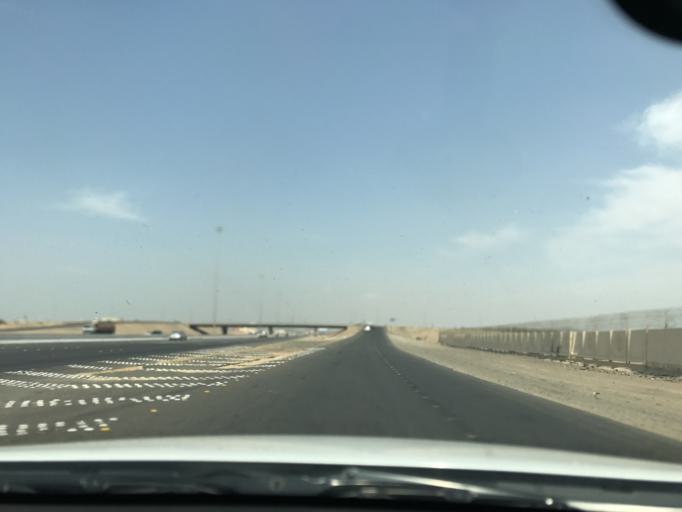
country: SA
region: Makkah
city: Jeddah
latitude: 21.3888
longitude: 39.4225
